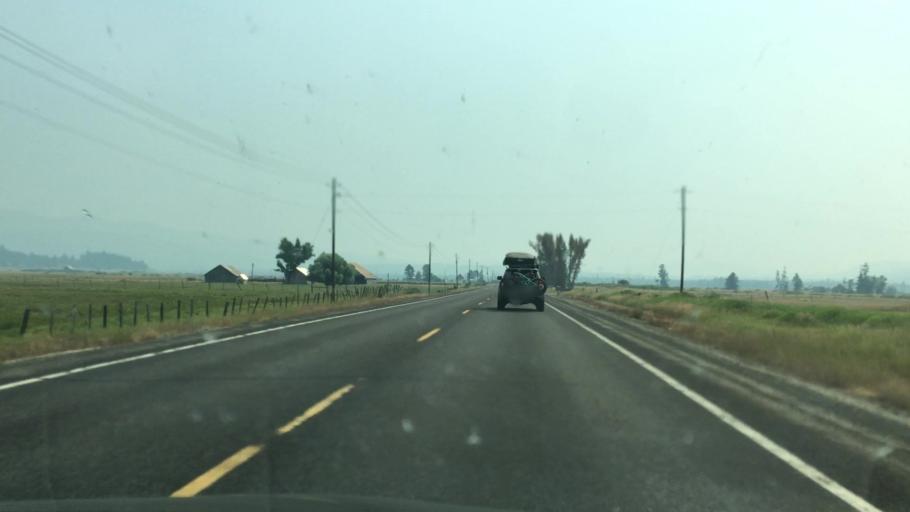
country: US
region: Idaho
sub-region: Valley County
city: Cascade
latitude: 44.4349
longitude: -115.9994
